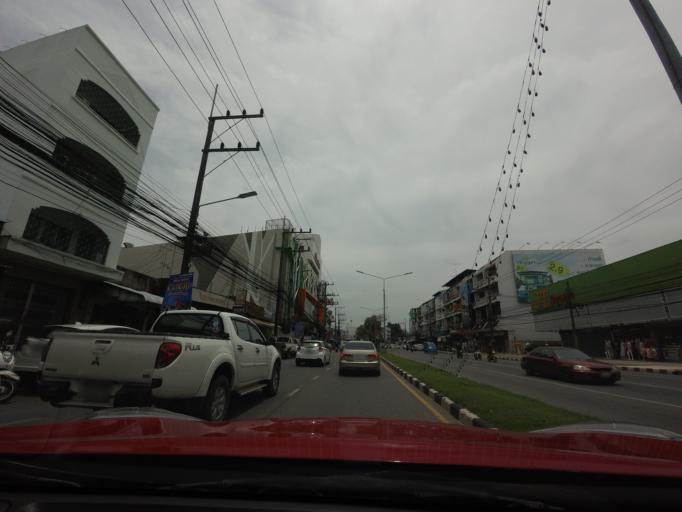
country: TH
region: Songkhla
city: Hat Yai
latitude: 6.9983
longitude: 100.4794
